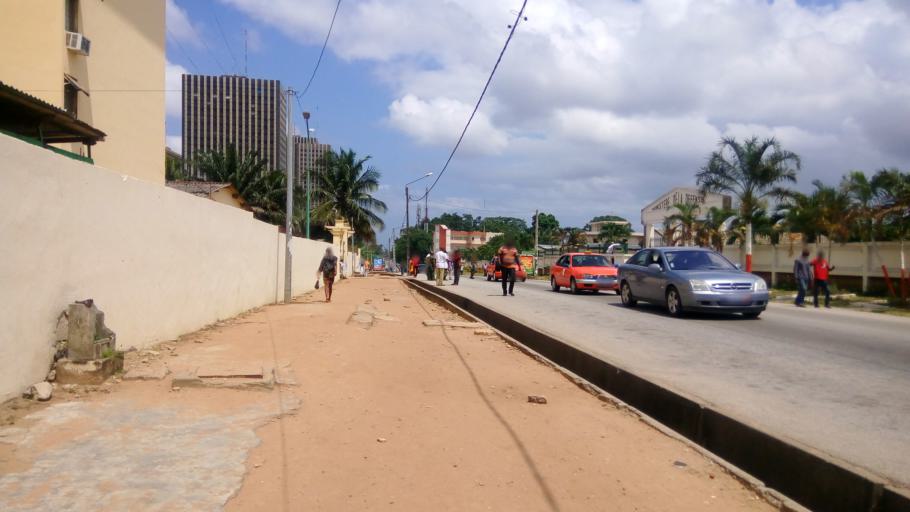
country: CI
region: Lagunes
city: Abidjan
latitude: 5.3383
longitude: -4.0237
